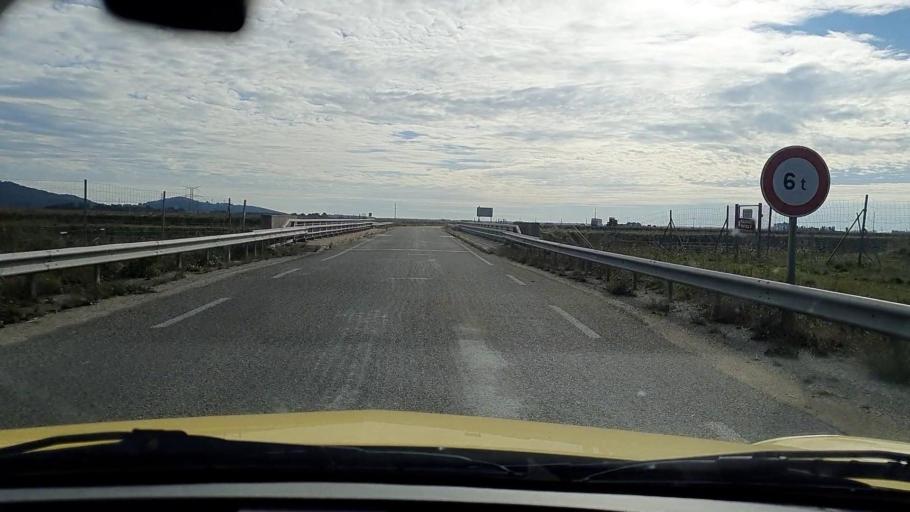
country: FR
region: Languedoc-Roussillon
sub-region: Departement du Gard
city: Jonquieres-Saint-Vincent
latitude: 43.8538
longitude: 4.5754
